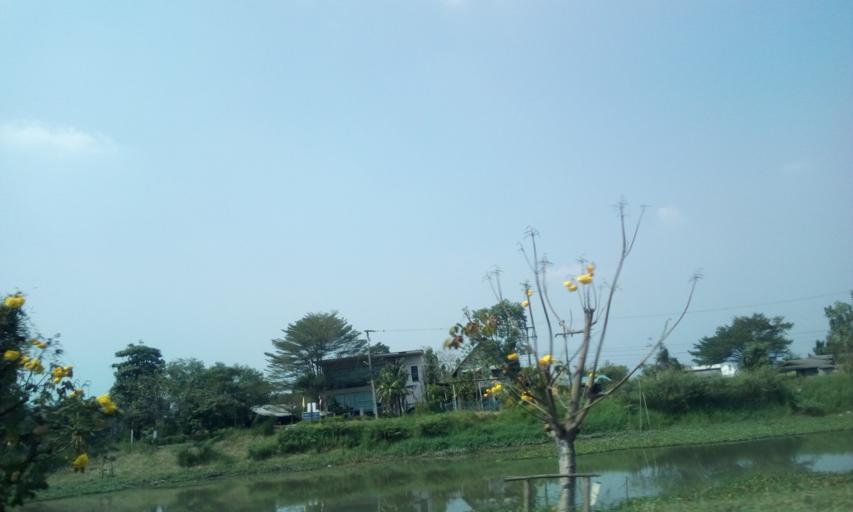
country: TH
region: Nakhon Nayok
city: Ongkharak
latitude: 14.1492
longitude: 100.9887
